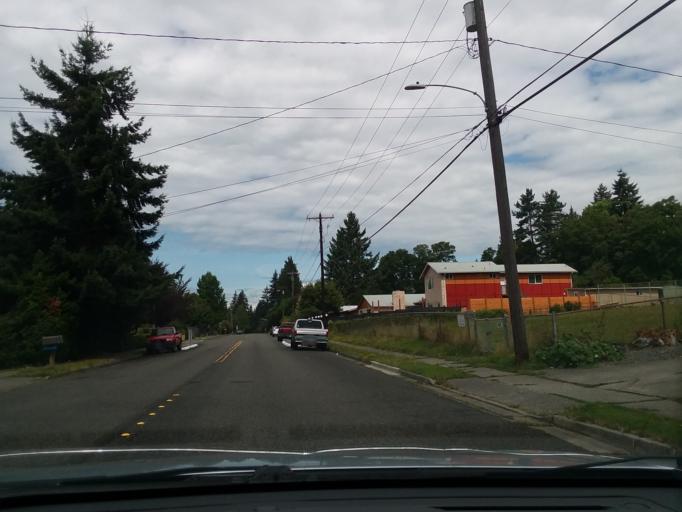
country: US
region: Washington
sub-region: Snohomish County
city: Alderwood Manor
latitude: 47.8291
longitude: -122.2978
